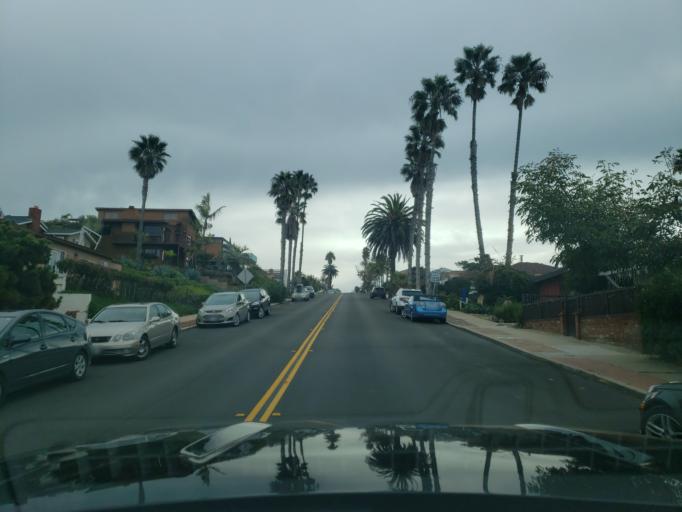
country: US
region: California
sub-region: San Diego County
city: Coronado
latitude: 32.7381
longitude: -117.2472
